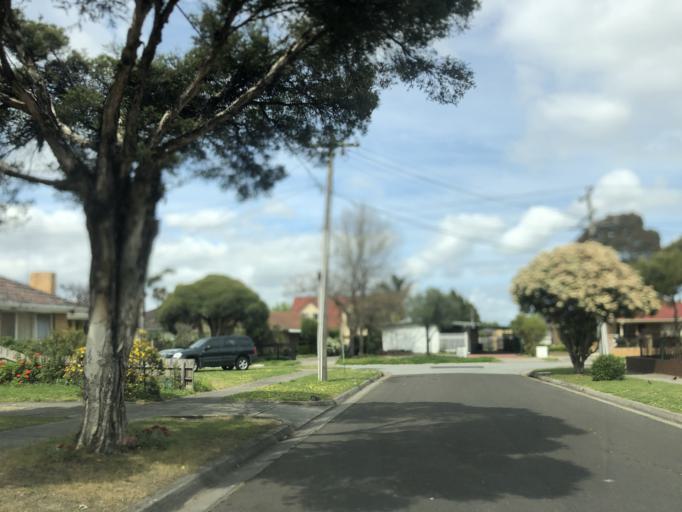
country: AU
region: Victoria
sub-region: Greater Dandenong
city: Dandenong North
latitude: -37.9568
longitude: 145.2101
